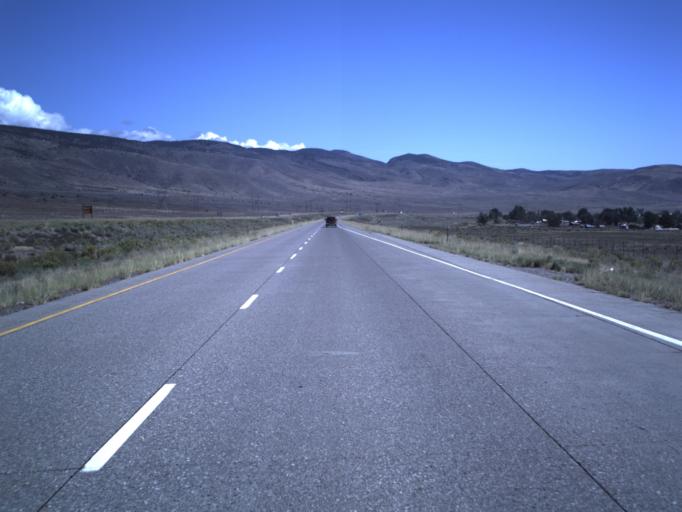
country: US
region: Utah
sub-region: Sevier County
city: Monroe
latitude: 38.6334
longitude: -112.2226
